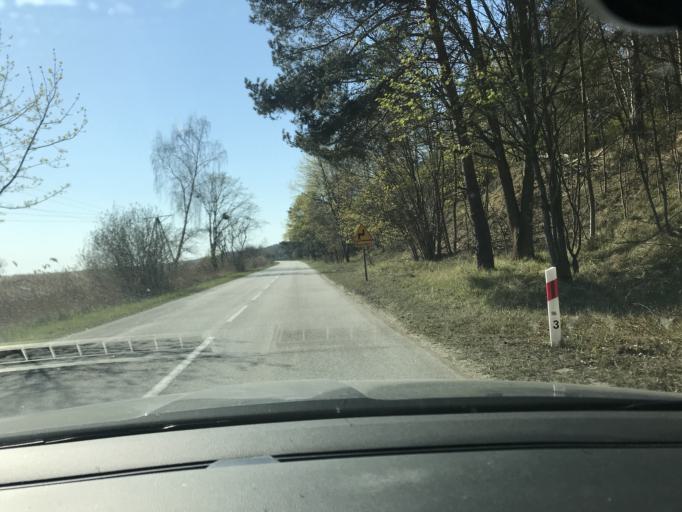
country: PL
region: Pomeranian Voivodeship
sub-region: Powiat nowodworski
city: Sztutowo
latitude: 54.3526
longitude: 19.3027
